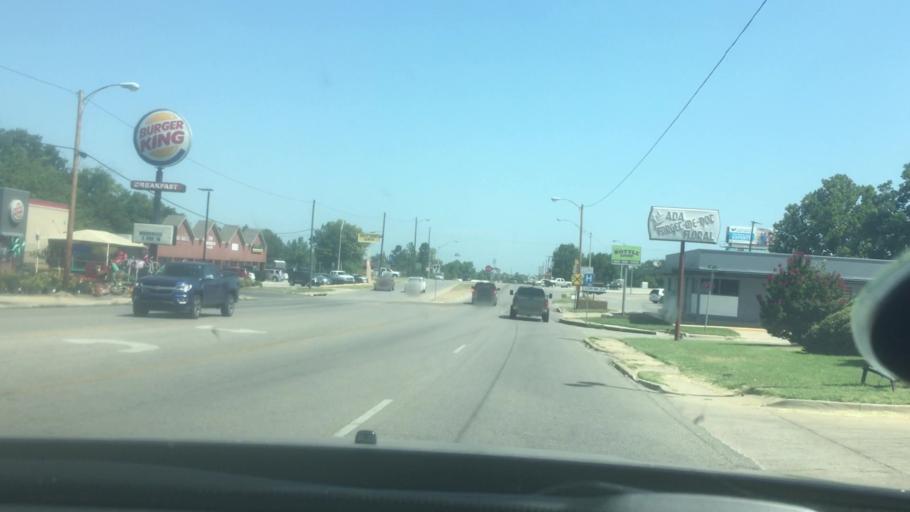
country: US
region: Oklahoma
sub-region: Pontotoc County
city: Ada
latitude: 34.7799
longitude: -96.6699
